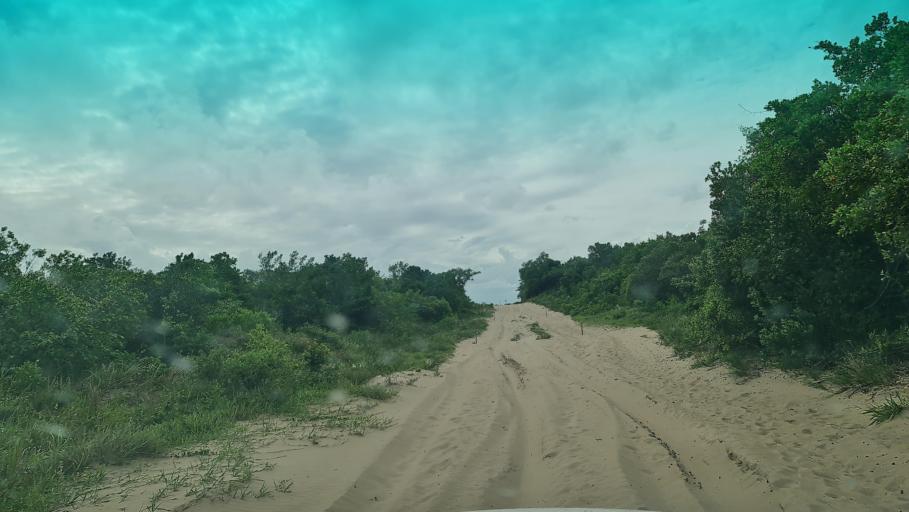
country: MZ
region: Maputo
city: Manhica
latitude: -25.4336
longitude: 32.9080
